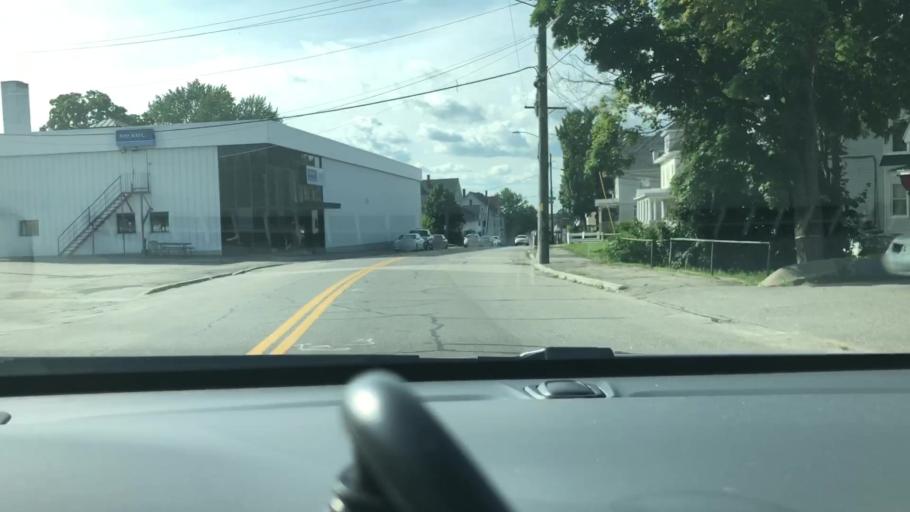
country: US
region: New Hampshire
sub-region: Hillsborough County
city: Manchester
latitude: 42.9833
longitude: -71.4408
